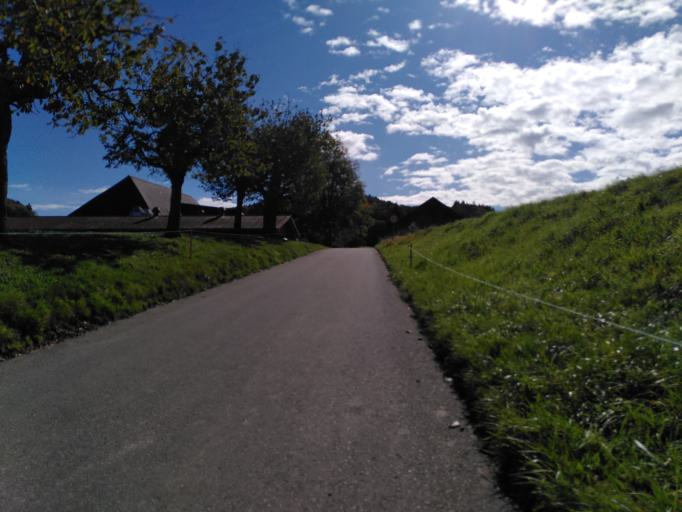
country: CH
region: Bern
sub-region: Oberaargau
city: Seeberg
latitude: 47.1357
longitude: 7.7164
